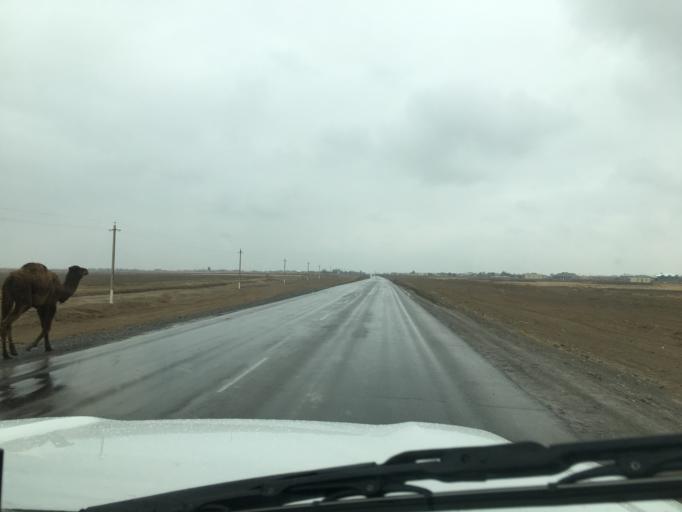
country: TM
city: Murgab
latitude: 37.4645
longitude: 62.0424
